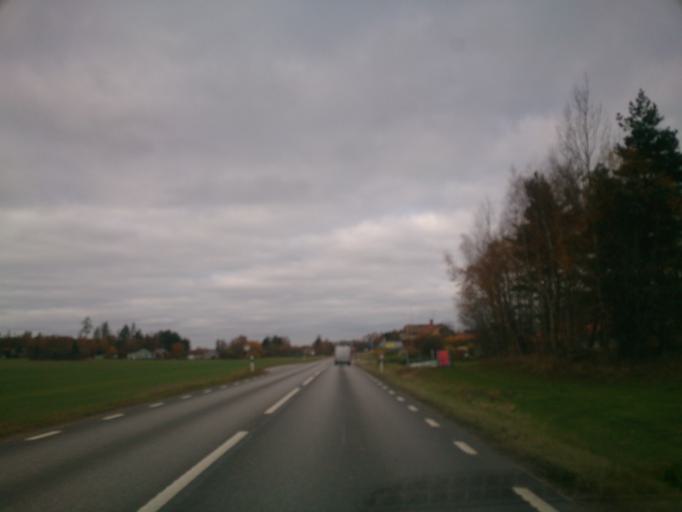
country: SE
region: OEstergoetland
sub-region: Linkopings Kommun
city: Linghem
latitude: 58.3796
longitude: 15.7983
